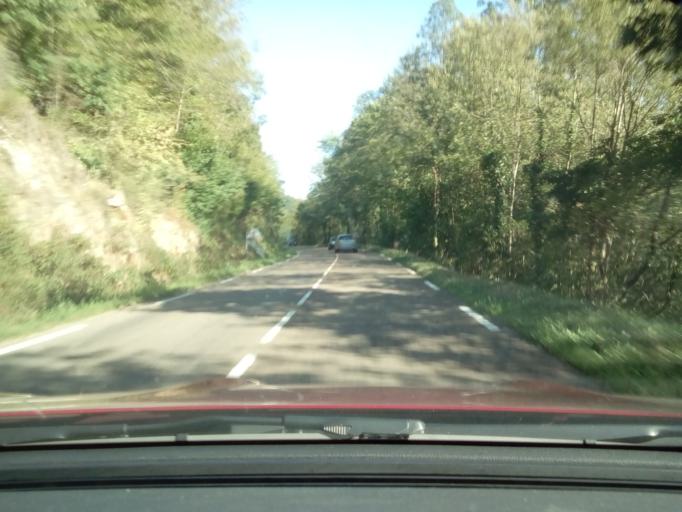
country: FR
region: Rhone-Alpes
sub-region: Departement du Rhone
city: Saint-Verand
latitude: 45.9064
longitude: 4.5228
